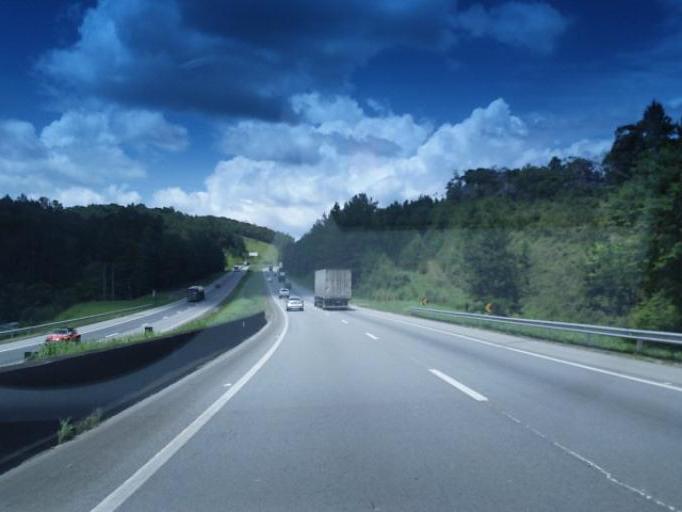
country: BR
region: Sao Paulo
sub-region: Juquitiba
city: Juquitiba
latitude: -23.9678
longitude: -47.1325
